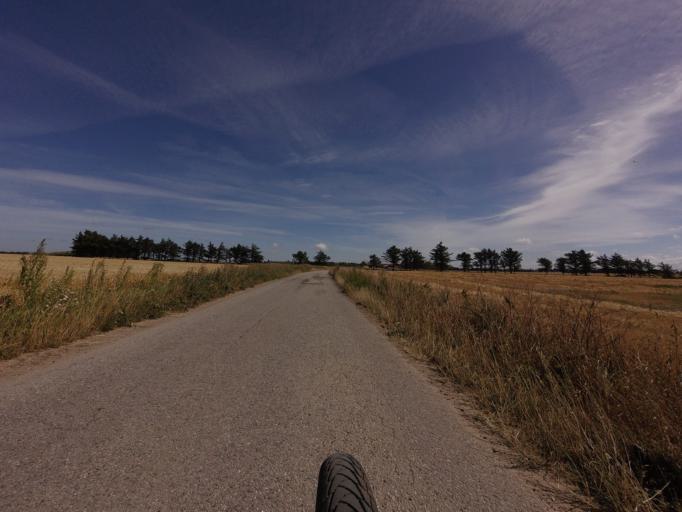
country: DK
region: North Denmark
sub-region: Hjorring Kommune
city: Vra
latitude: 57.3870
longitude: 9.8038
